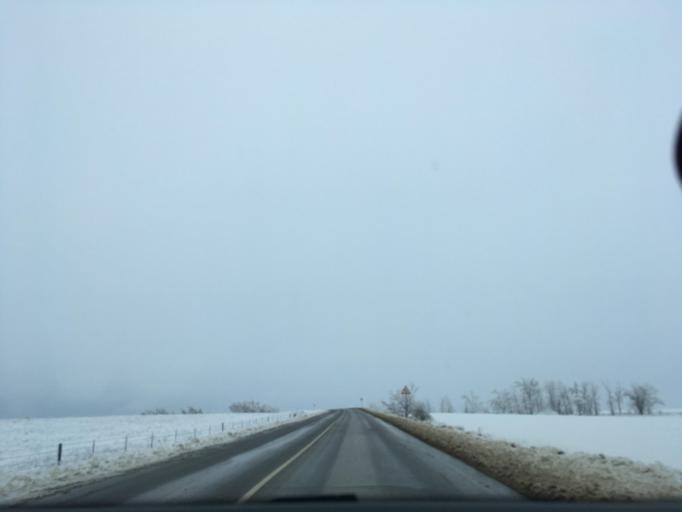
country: RU
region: Voronezj
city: Ol'khovatka
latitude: 50.2203
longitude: 39.2713
